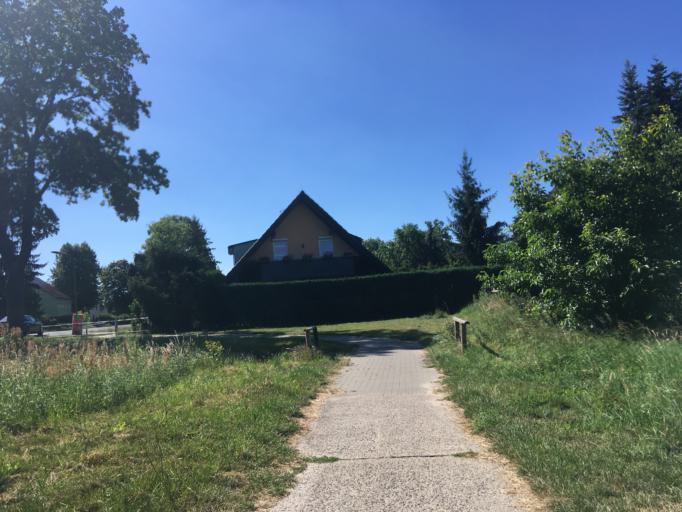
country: DE
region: Brandenburg
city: Petershagen
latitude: 52.5156
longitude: 13.7705
